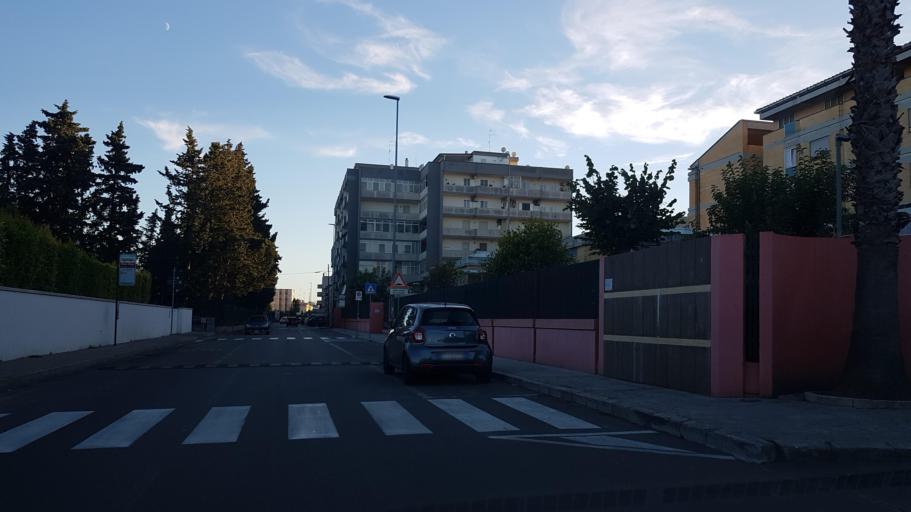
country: IT
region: Apulia
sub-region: Provincia di Lecce
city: Lecce
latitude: 40.3680
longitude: 18.1769
